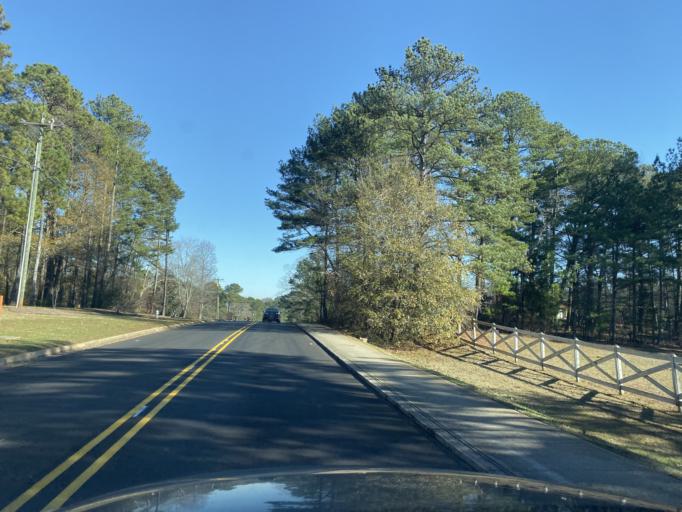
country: US
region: Georgia
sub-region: DeKalb County
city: Pine Mountain
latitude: 33.6765
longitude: -84.1637
